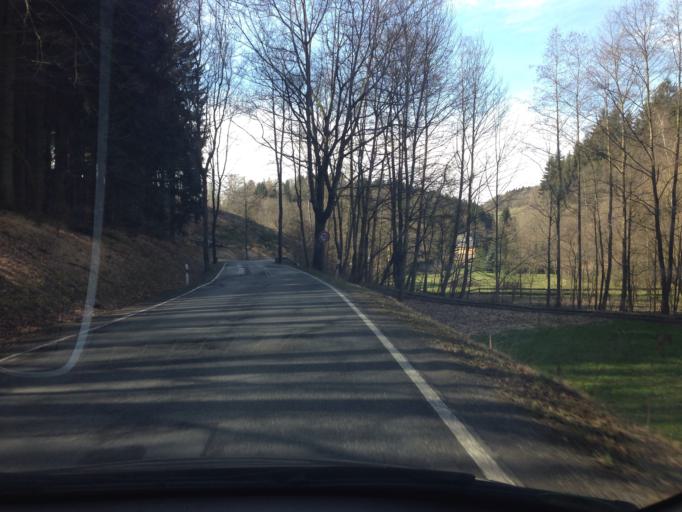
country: DE
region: Saxony
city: Scharfenstein
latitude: 50.7050
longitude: 13.0437
